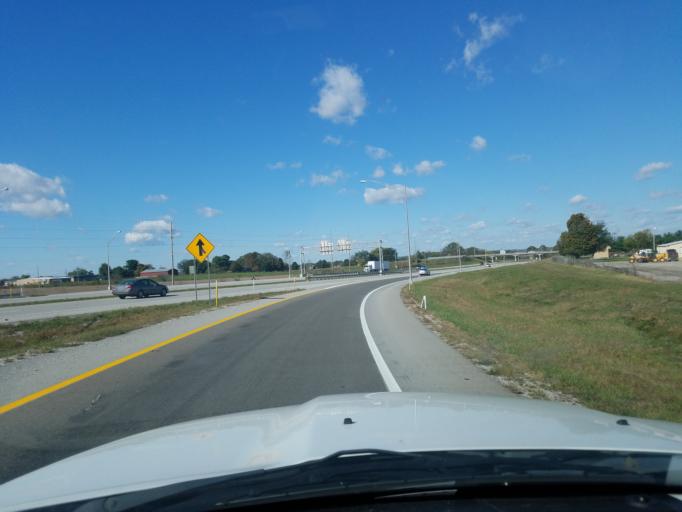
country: US
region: Kentucky
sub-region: Warren County
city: Plano
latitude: 36.9119
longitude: -86.4355
